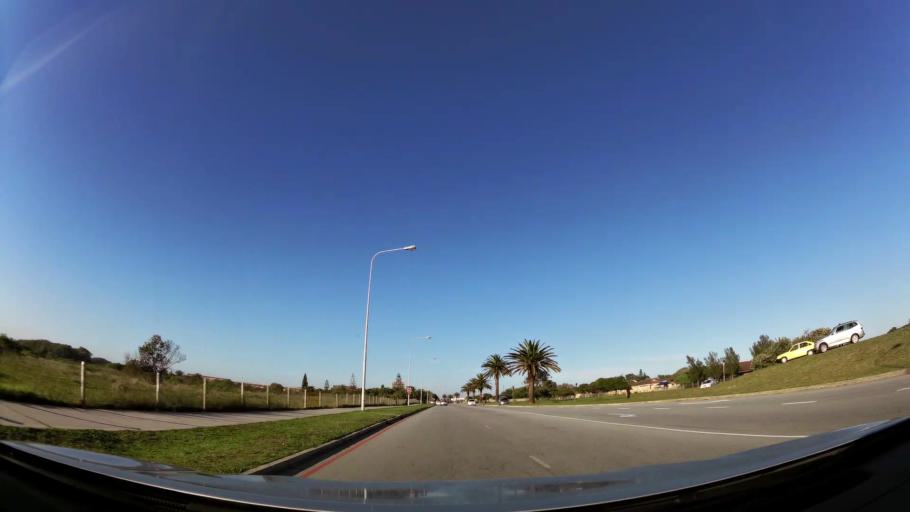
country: ZA
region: Eastern Cape
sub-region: Nelson Mandela Bay Metropolitan Municipality
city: Port Elizabeth
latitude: -33.9960
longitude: 25.6706
